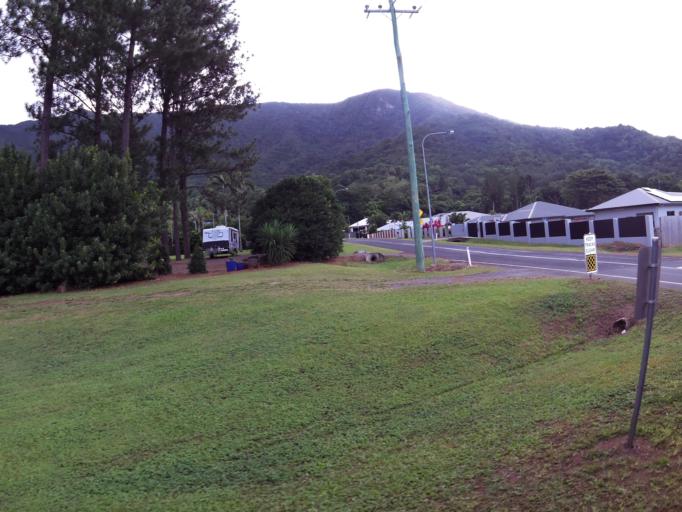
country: AU
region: Queensland
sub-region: Cairns
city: Redlynch
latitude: -16.9013
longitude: 145.6921
